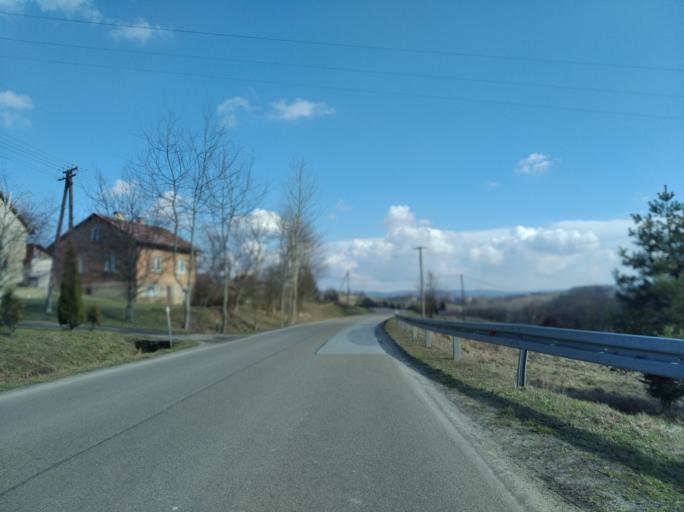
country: PL
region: Subcarpathian Voivodeship
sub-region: Powiat strzyzowski
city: Frysztak
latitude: 49.8472
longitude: 21.5515
